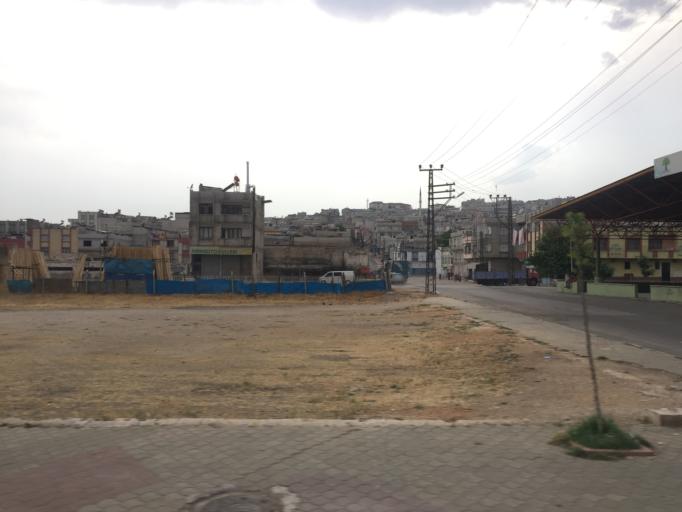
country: TR
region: Gaziantep
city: Gaziantep
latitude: 37.0691
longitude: 37.4139
